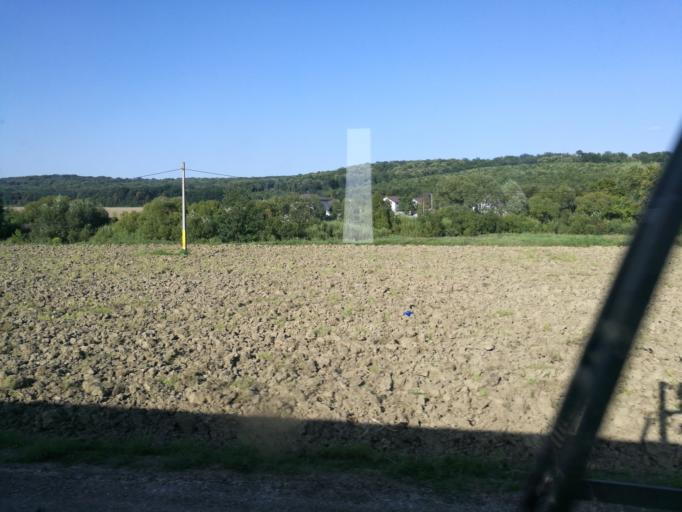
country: RO
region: Iasi
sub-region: Comuna Grajduri
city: Grajduri
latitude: 46.9585
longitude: 27.5570
